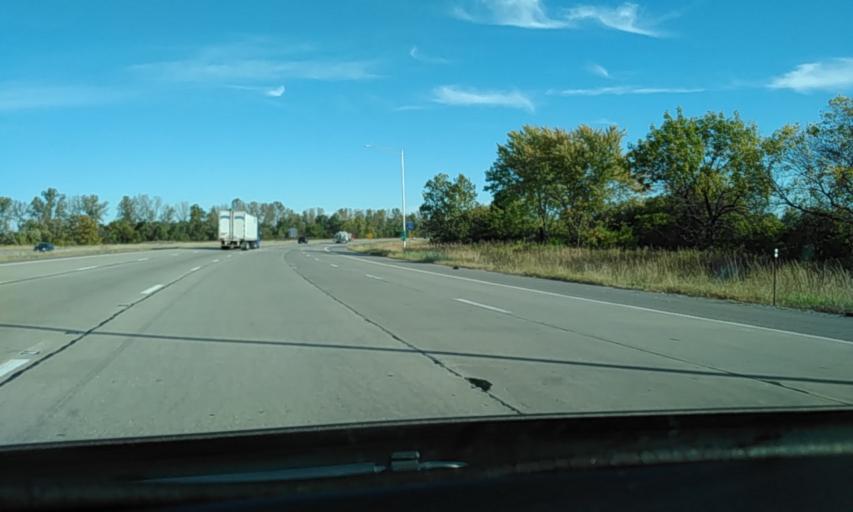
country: US
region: Illinois
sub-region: Saint Clair County
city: Washington Park
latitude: 38.6277
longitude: -90.0671
